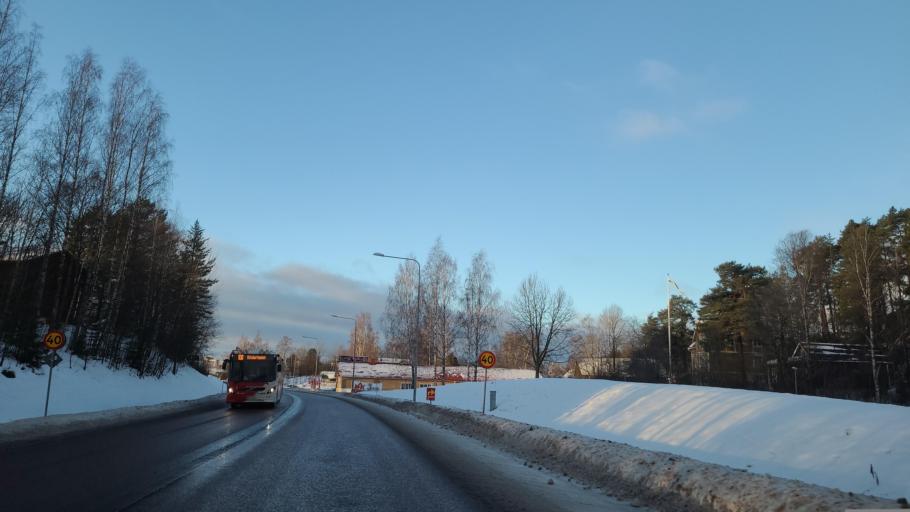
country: SE
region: Gaevleborg
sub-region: Bollnas Kommun
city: Bollnas
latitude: 61.3566
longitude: 16.4163
